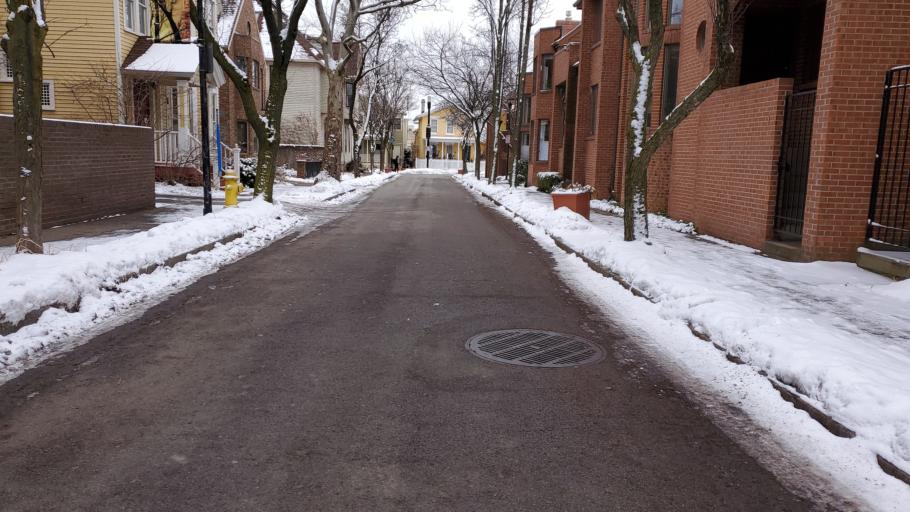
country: US
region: New York
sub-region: Monroe County
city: Rochester
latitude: 43.1599
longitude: -77.6005
